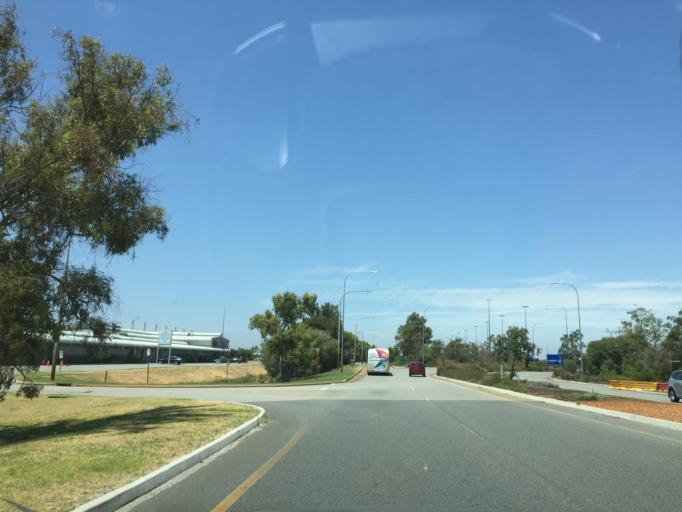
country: AU
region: Western Australia
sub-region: Belmont
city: Redcliffe
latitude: -31.9470
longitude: 115.9741
